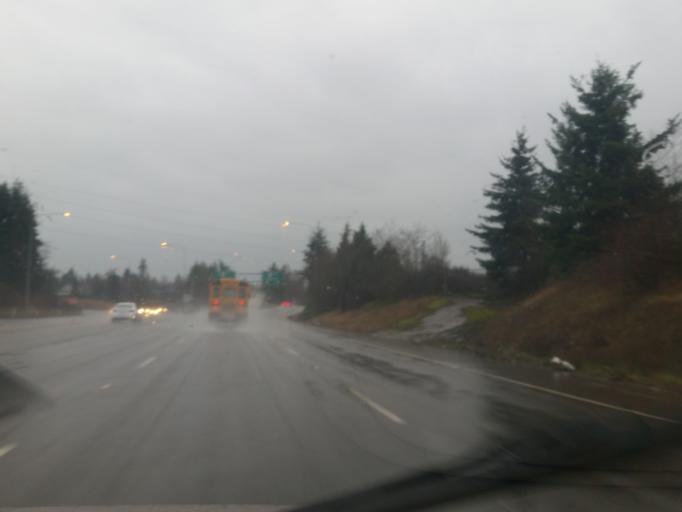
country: US
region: Washington
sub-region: Snohomish County
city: Mukilteo
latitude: 47.9259
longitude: -122.2608
